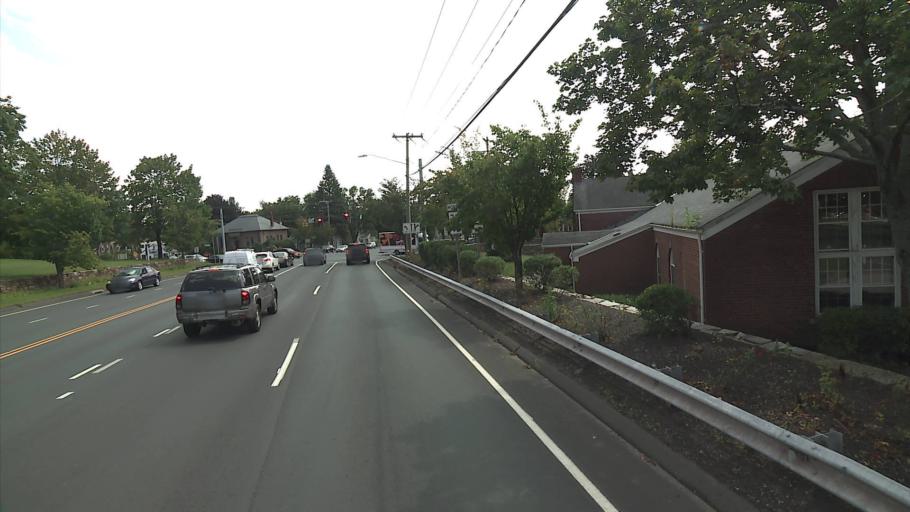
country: US
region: Connecticut
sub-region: Hartford County
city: Manchester
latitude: 41.8274
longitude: -72.5537
